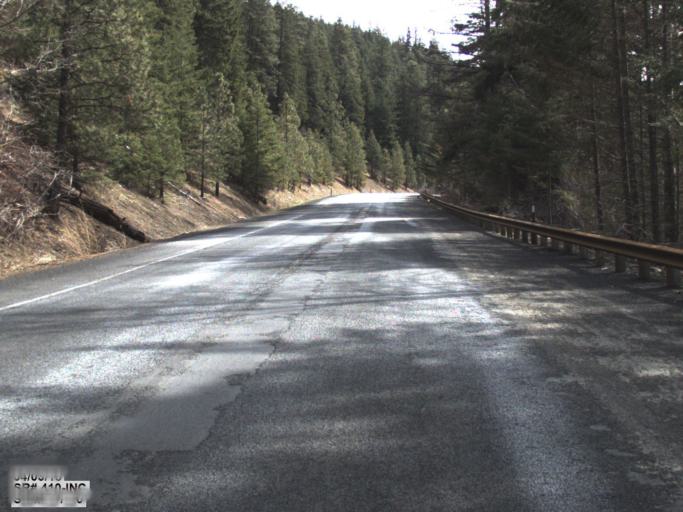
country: US
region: Washington
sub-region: Kittitas County
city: Cle Elum
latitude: 46.9301
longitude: -121.0500
